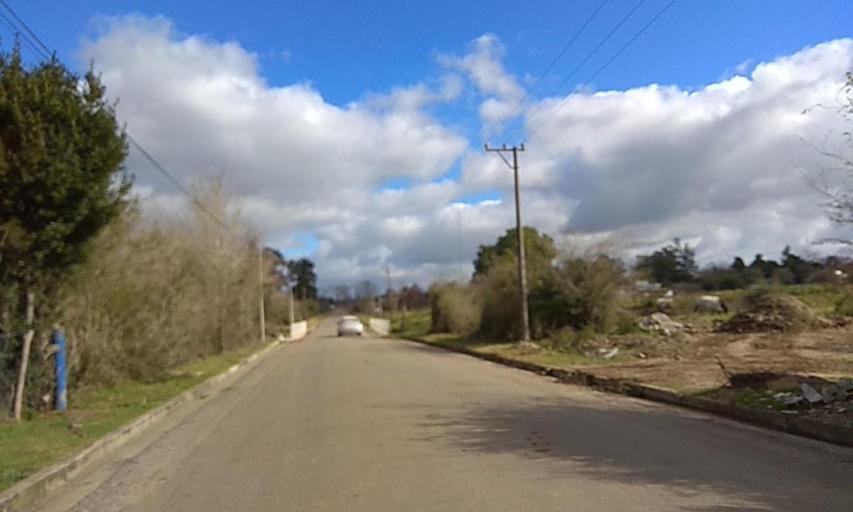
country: UY
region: Florida
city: Florida
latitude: -34.1076
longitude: -56.2185
